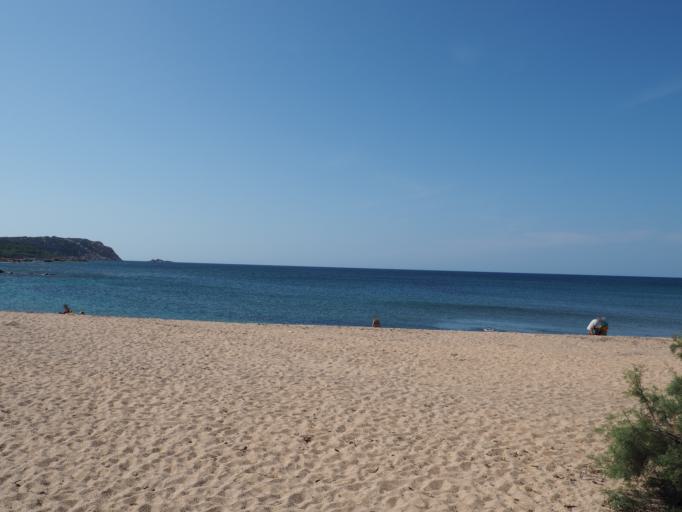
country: IT
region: Sardinia
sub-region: Provincia di Olbia-Tempio
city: Aglientu
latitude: 41.1557
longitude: 9.1534
